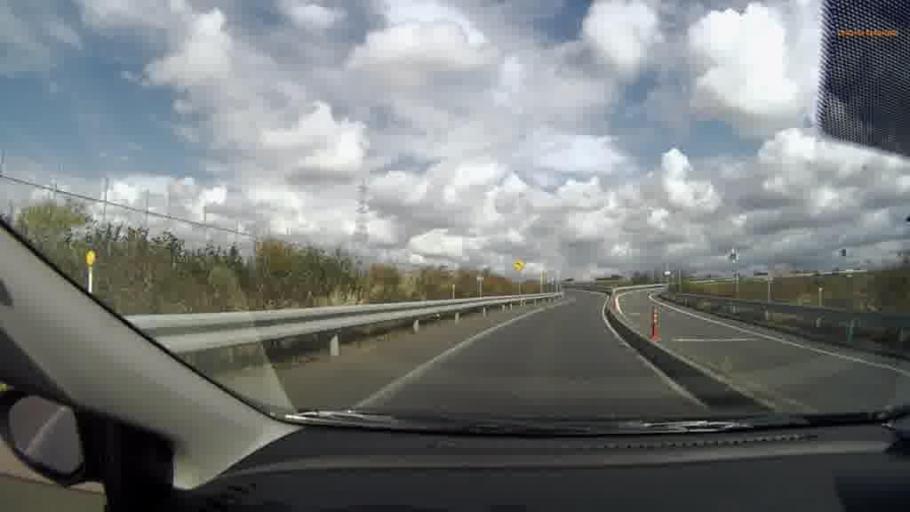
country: JP
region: Hokkaido
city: Kushiro
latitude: 43.0288
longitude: 144.4010
